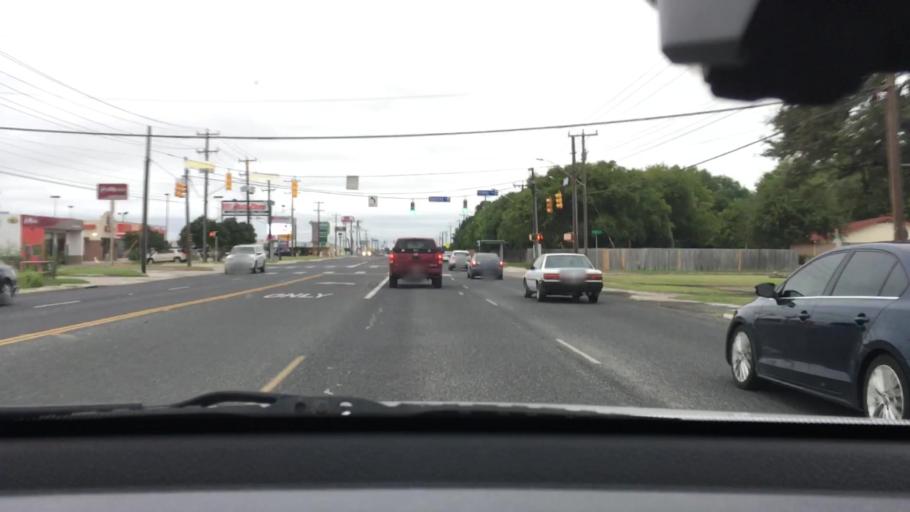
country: US
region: Texas
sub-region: Bexar County
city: Windcrest
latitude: 29.5103
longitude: -98.3764
